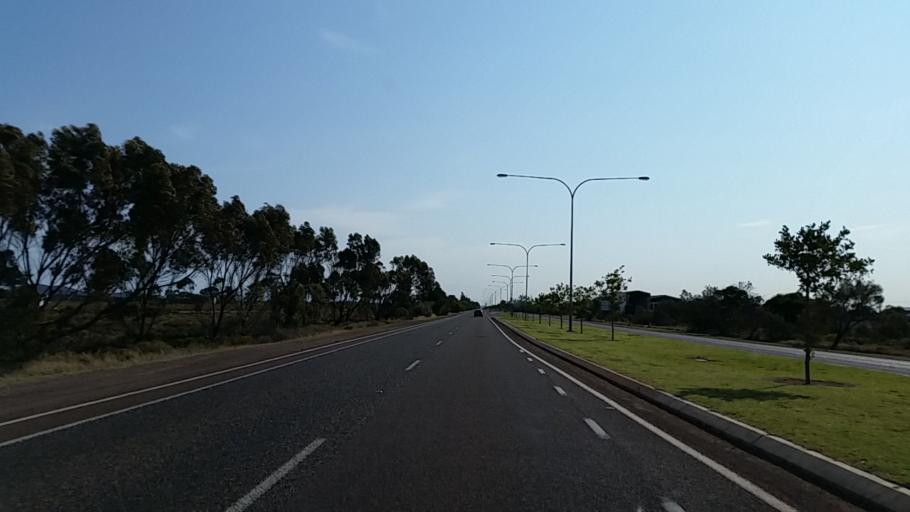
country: AU
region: South Australia
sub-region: Whyalla
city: Whyalla
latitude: -33.0407
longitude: 137.5515
